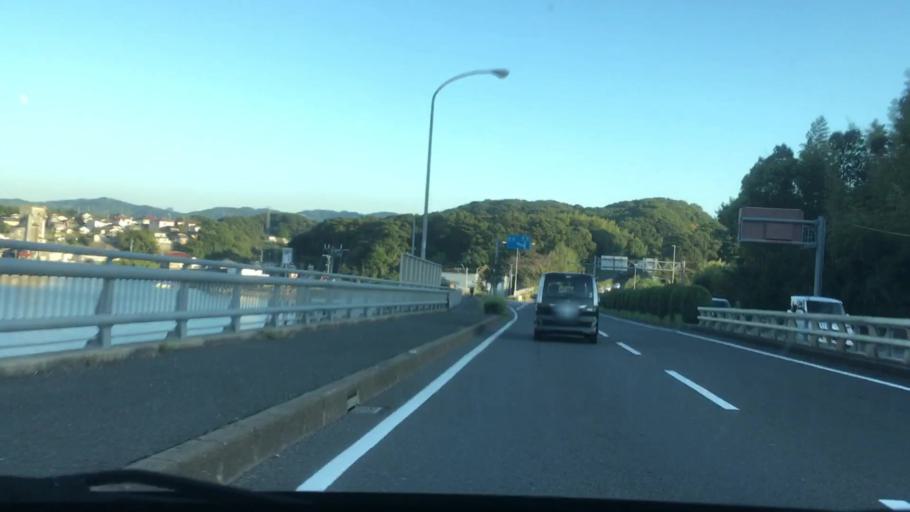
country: JP
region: Nagasaki
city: Sasebo
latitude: 33.1416
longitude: 129.7825
